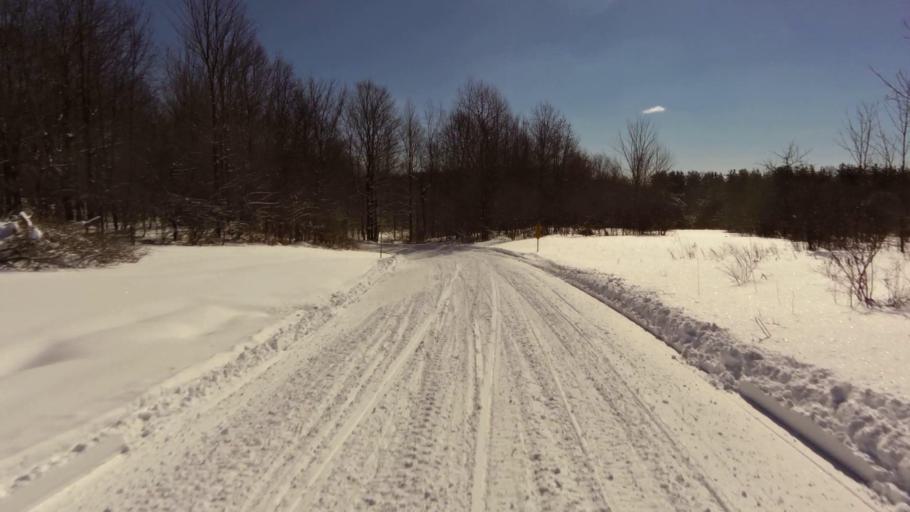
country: US
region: New York
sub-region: Chautauqua County
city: Mayville
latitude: 42.2316
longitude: -79.3927
